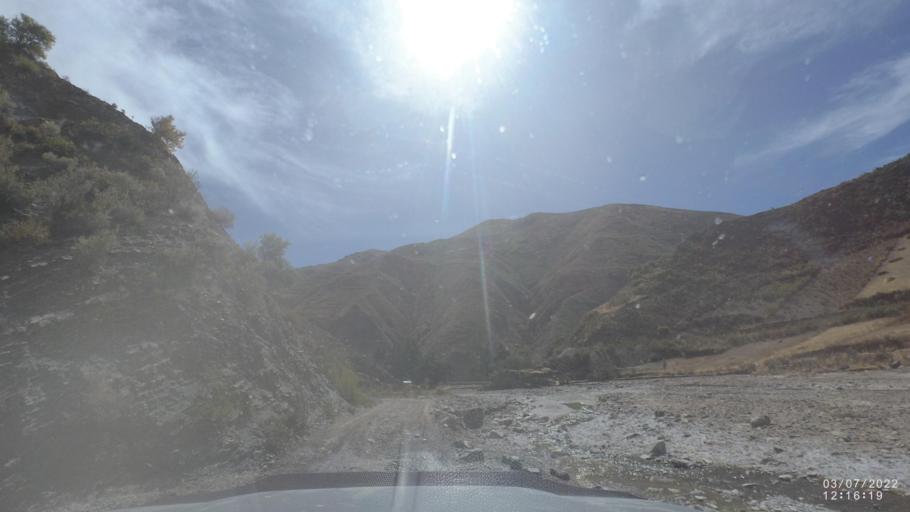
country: BO
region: Cochabamba
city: Irpa Irpa
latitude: -17.8262
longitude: -66.6067
